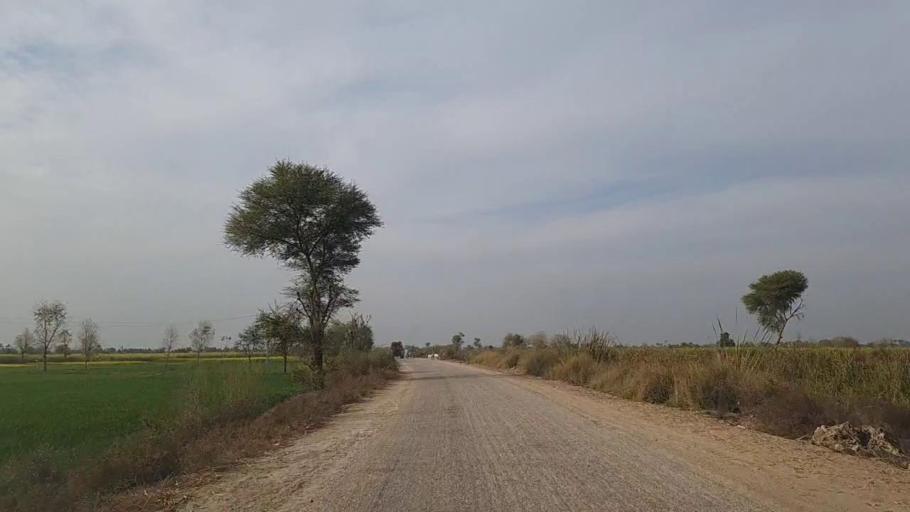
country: PK
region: Sindh
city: Daur
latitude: 26.4871
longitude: 68.4629
